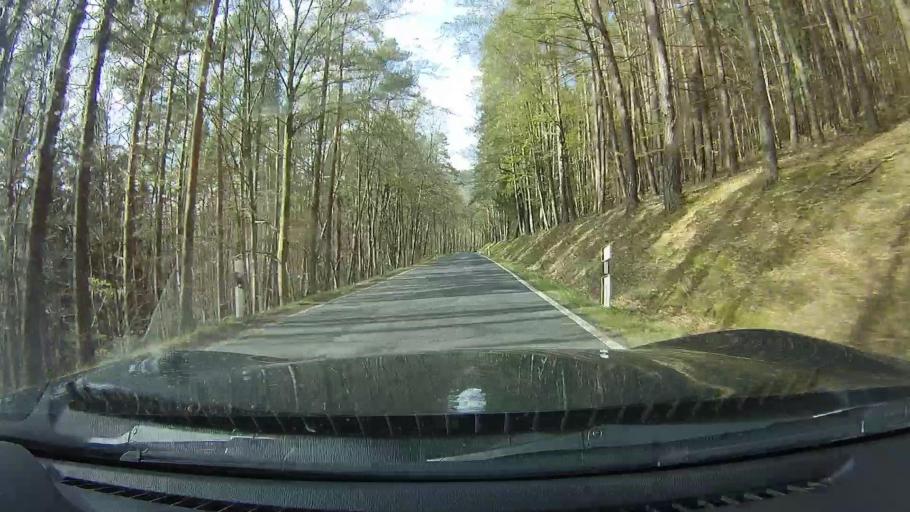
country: DE
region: Bavaria
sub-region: Regierungsbezirk Unterfranken
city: Weilbach
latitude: 49.6323
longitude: 9.2517
